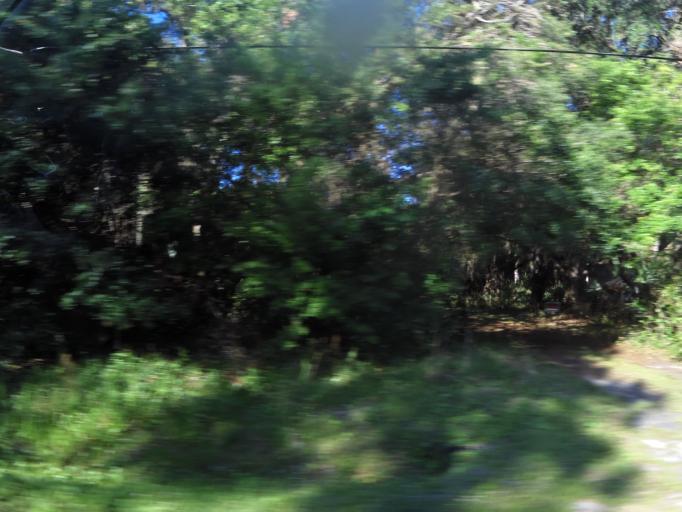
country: US
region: Florida
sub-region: Duval County
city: Atlantic Beach
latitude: 30.4535
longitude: -81.4661
